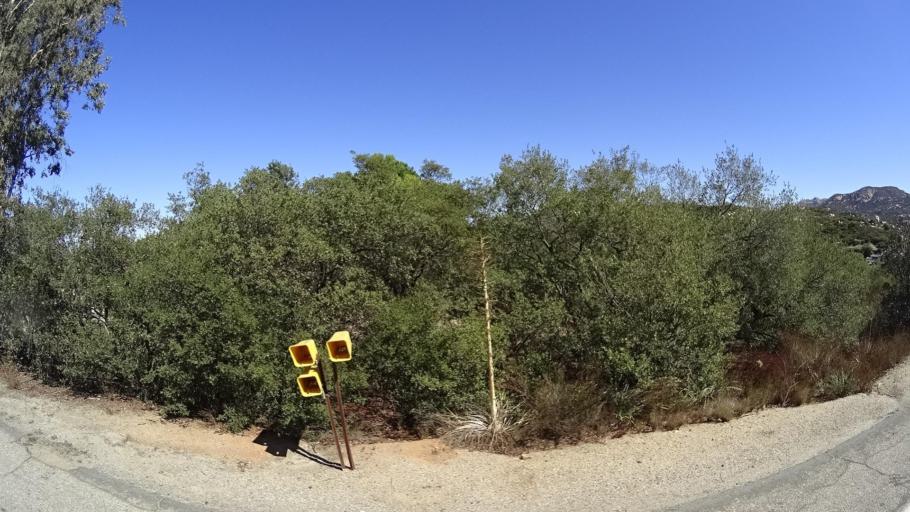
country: US
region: California
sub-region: San Diego County
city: Jamul
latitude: 32.7256
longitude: -116.7680
